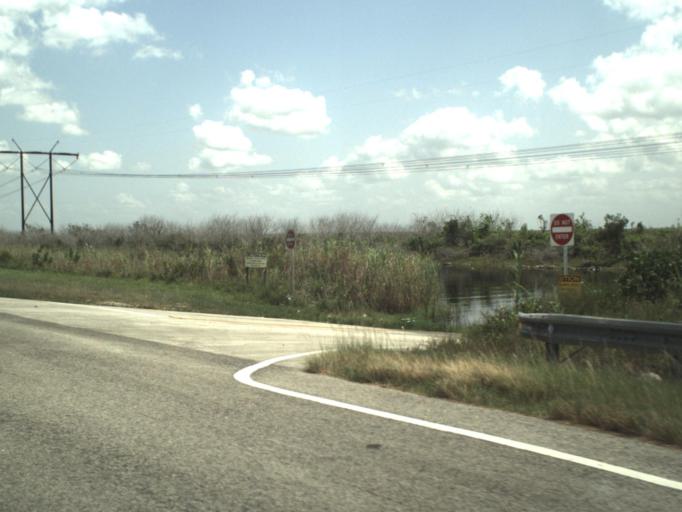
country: US
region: Florida
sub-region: Broward County
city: Weston
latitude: 26.1802
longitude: -80.4495
